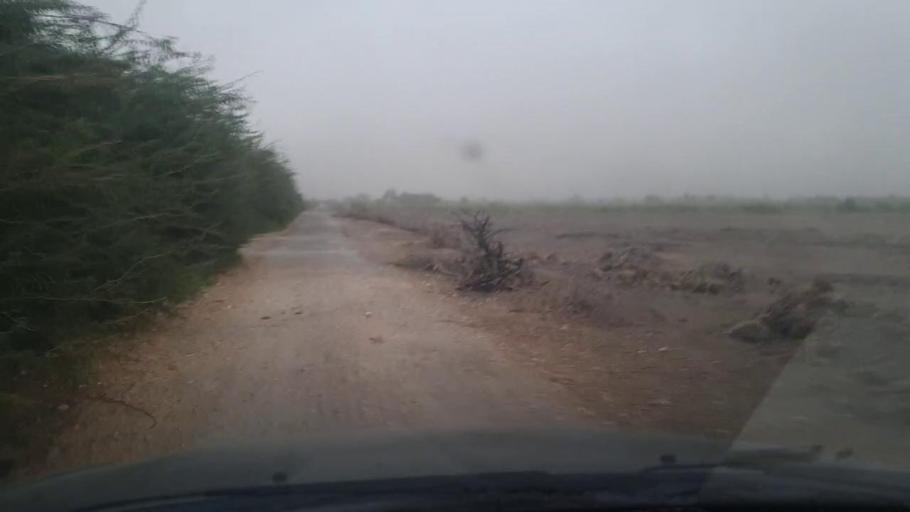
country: PK
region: Sindh
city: Digri
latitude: 25.0020
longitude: 69.1015
